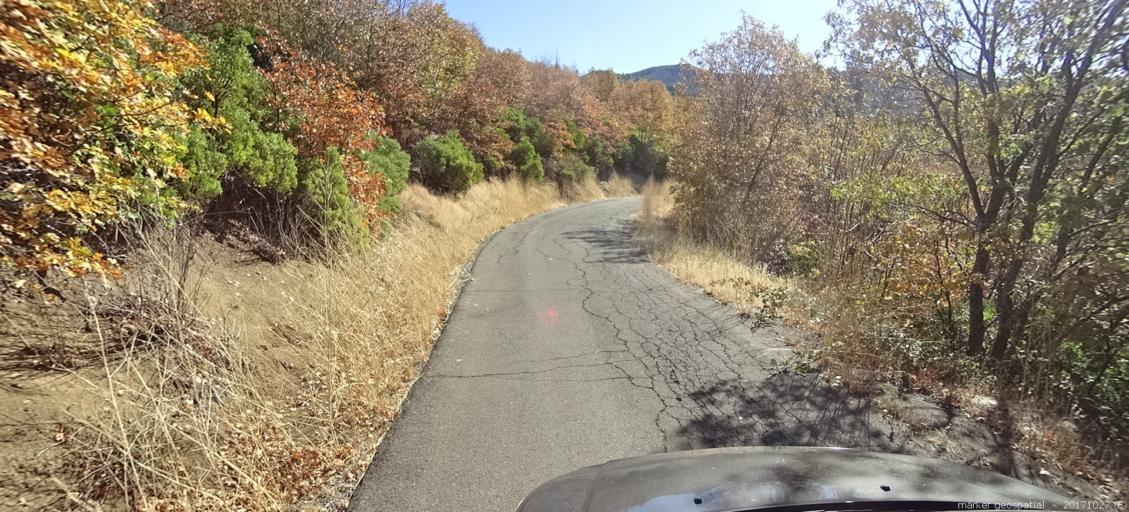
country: US
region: California
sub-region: Shasta County
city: Burney
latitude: 40.8003
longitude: -121.8966
